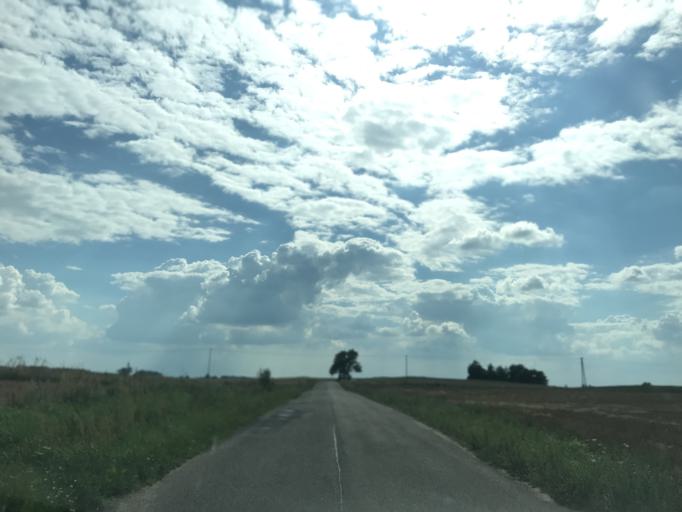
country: PL
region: Kujawsko-Pomorskie
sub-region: Powiat brodnicki
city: Brzozie
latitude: 53.3391
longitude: 19.6666
